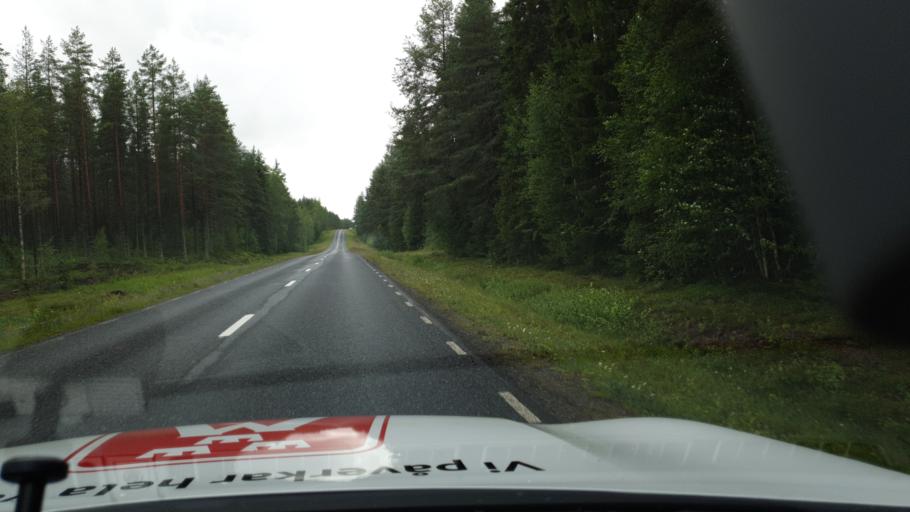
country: SE
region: Vaesterbotten
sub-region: Skelleftea Kommun
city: Storvik
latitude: 64.9684
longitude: 20.6737
